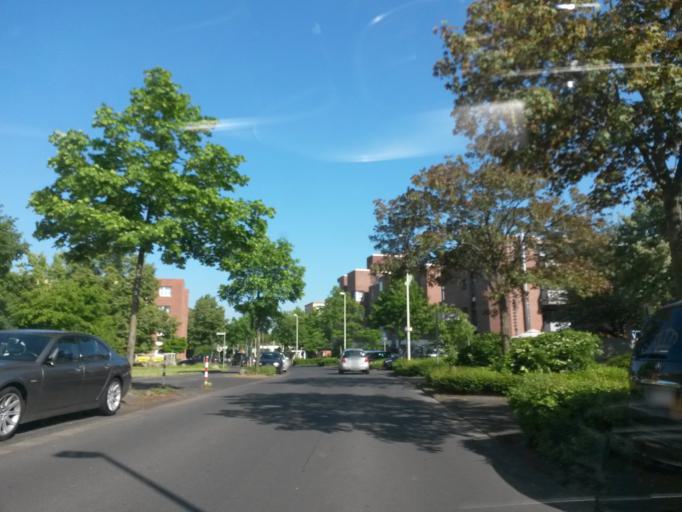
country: DE
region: North Rhine-Westphalia
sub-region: Regierungsbezirk Koln
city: Alfter
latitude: 50.6998
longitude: 7.0557
